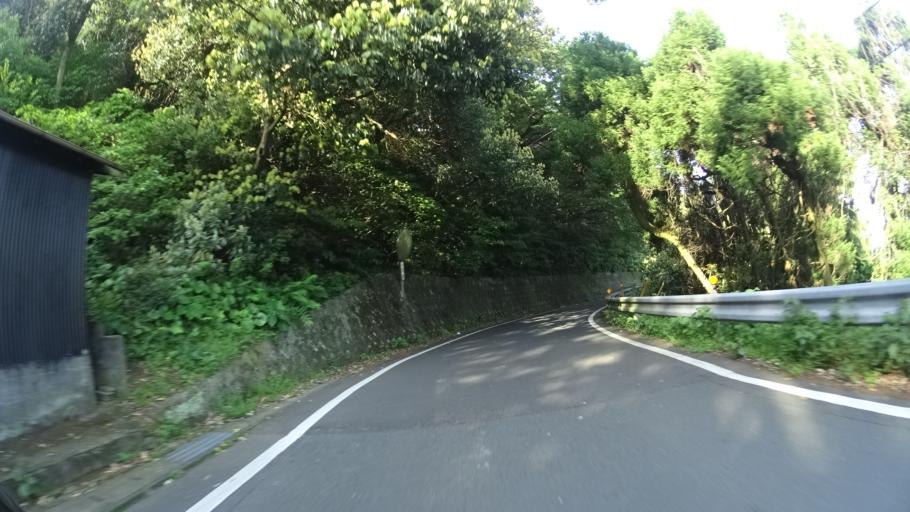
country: JP
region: Ehime
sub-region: Nishiuwa-gun
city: Ikata-cho
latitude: 33.3808
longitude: 132.0699
